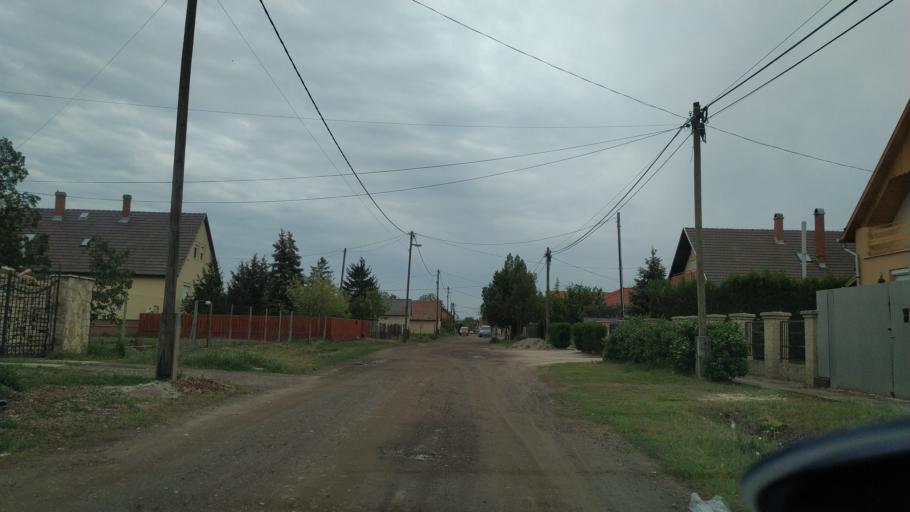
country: HU
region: Pest
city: Nagykata
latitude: 47.4235
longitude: 19.7280
